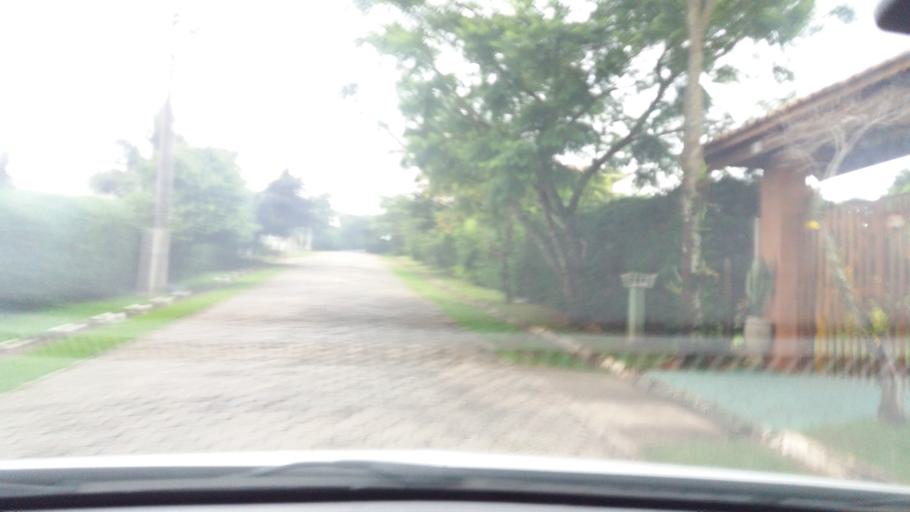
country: BR
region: Sao Paulo
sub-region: Bom Jesus Dos Perdoes
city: Bom Jesus dos Perdoes
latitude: -23.1662
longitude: -46.4622
